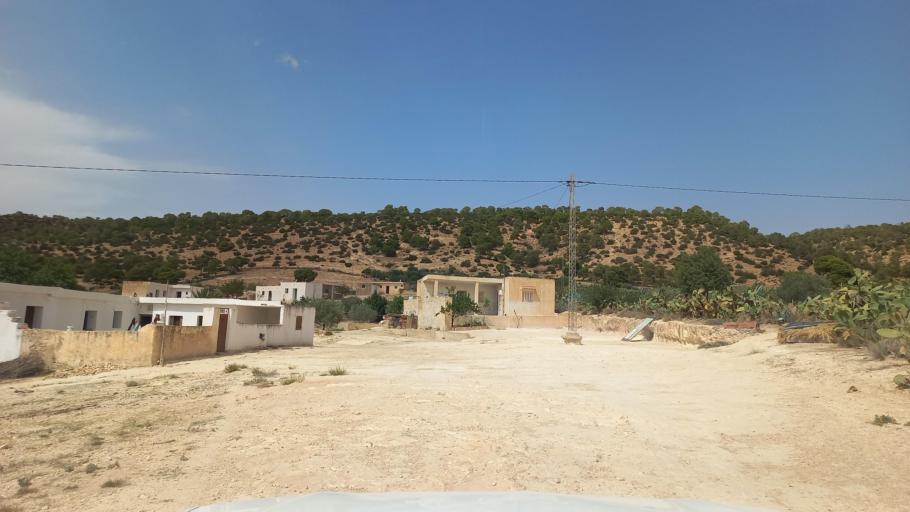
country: TN
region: Al Qasrayn
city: Kasserine
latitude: 35.3744
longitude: 8.9002
